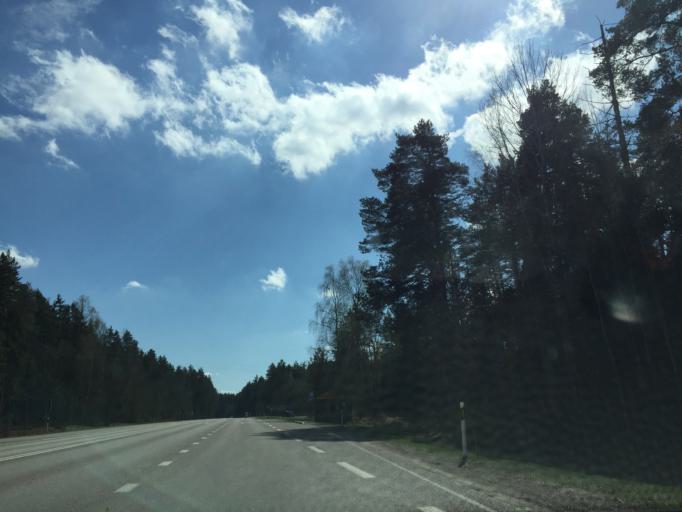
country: EE
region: Valgamaa
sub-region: Torva linn
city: Torva
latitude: 58.0116
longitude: 26.1629
